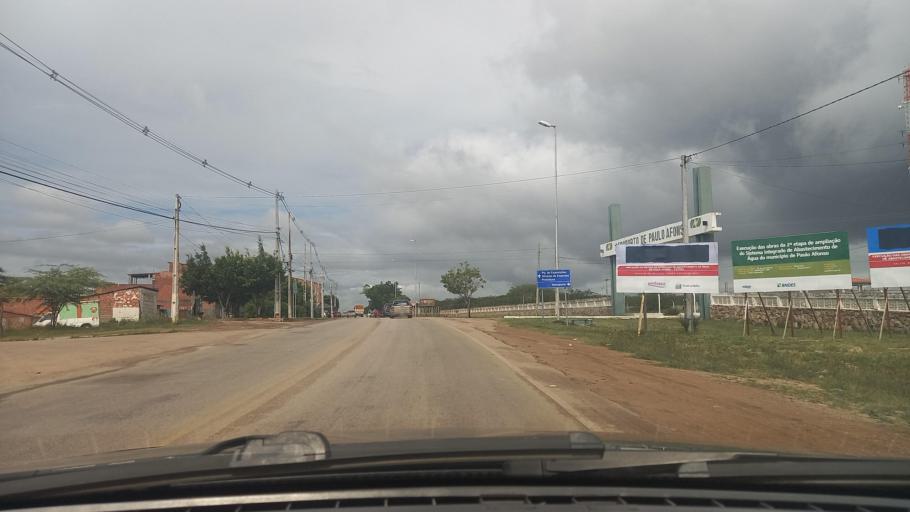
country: BR
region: Bahia
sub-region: Paulo Afonso
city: Paulo Afonso
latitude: -9.3961
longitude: -38.2482
